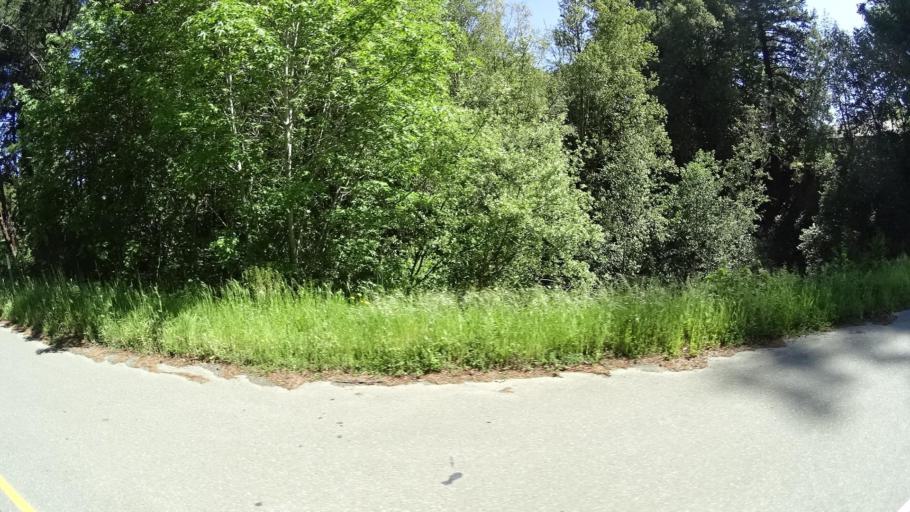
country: US
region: California
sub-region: Humboldt County
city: Rio Dell
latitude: 40.2517
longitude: -124.1831
